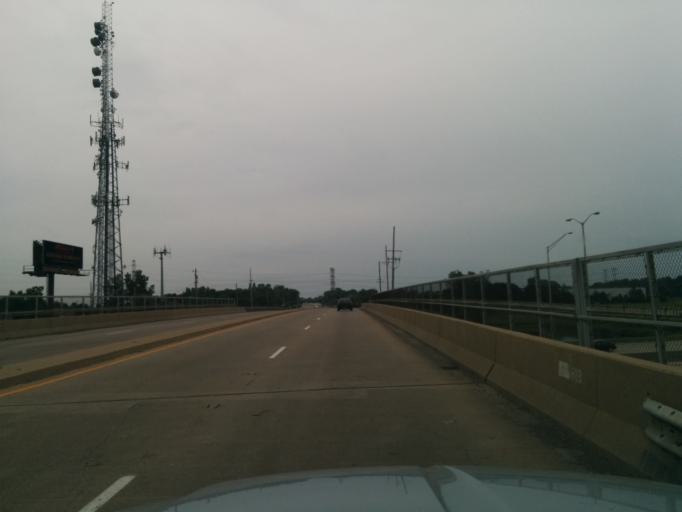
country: US
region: Illinois
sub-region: DuPage County
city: Warrenville
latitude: 41.8015
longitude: -88.2401
